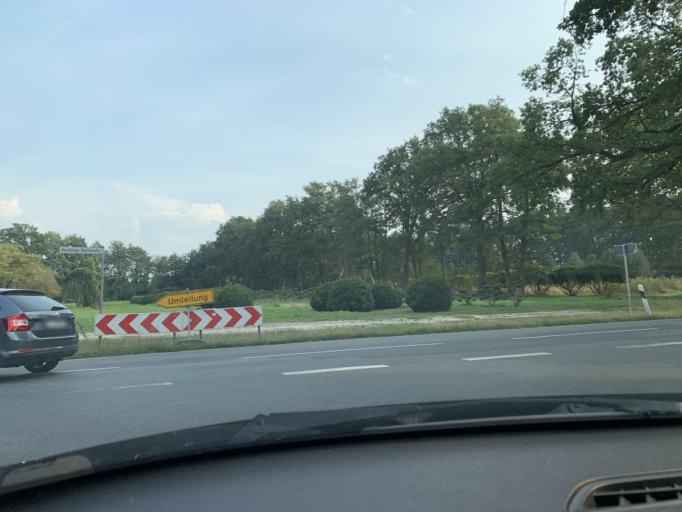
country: DE
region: Lower Saxony
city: Barssel
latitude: 53.1764
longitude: 7.7593
